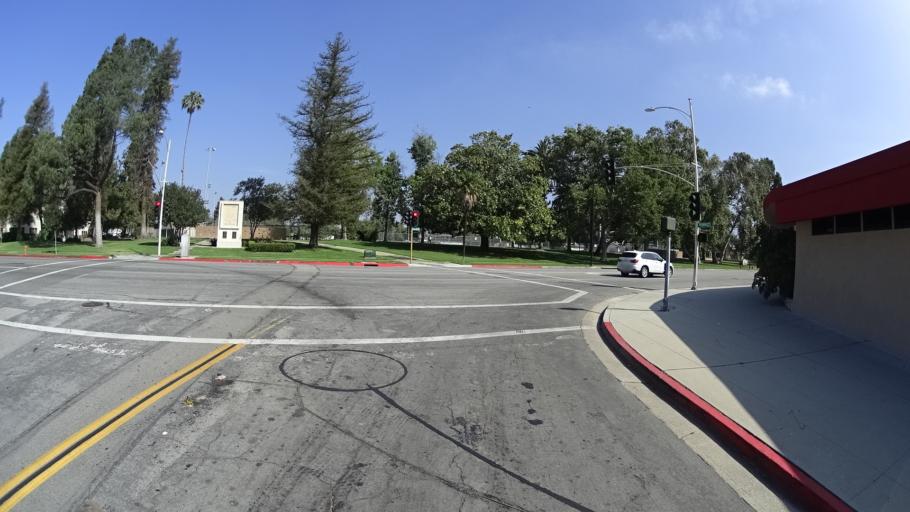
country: US
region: California
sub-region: Los Angeles County
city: Burbank
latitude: 34.1706
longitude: -118.3193
